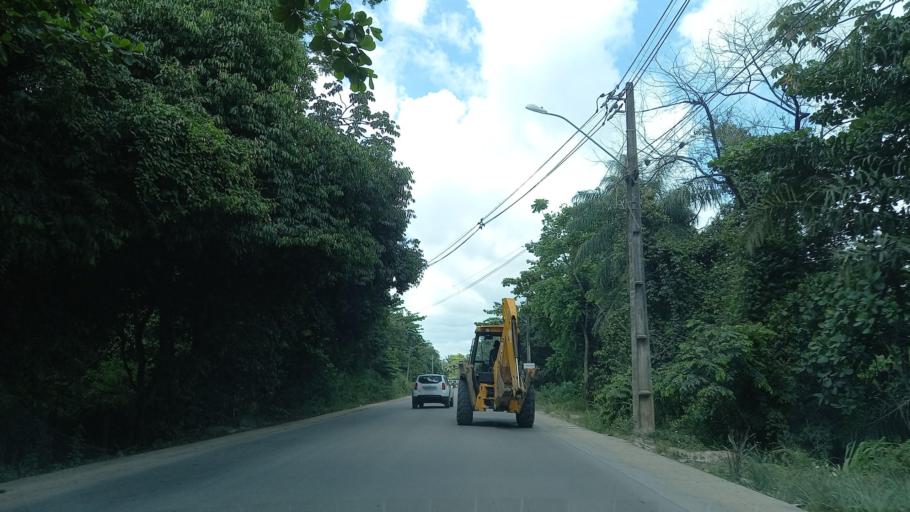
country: BR
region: Pernambuco
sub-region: Jaboatao Dos Guararapes
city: Jaboatao
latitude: -8.1598
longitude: -34.9826
